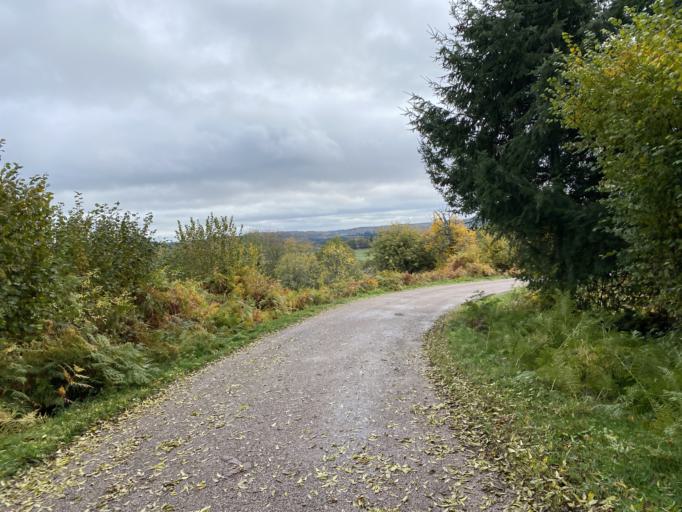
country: FR
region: Bourgogne
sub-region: Departement de la Cote-d'Or
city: Saulieu
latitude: 47.2645
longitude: 4.1694
